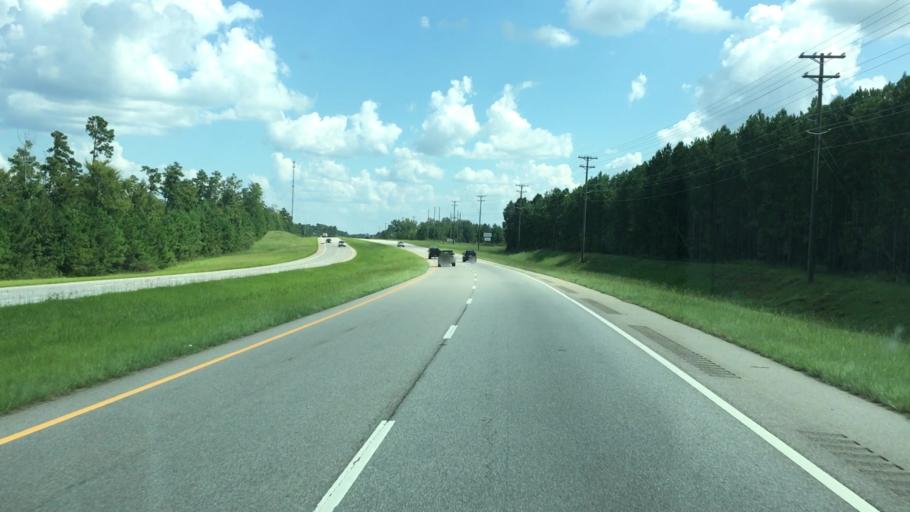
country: US
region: Georgia
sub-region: Putnam County
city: Eatonton
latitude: 33.2171
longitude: -83.3056
